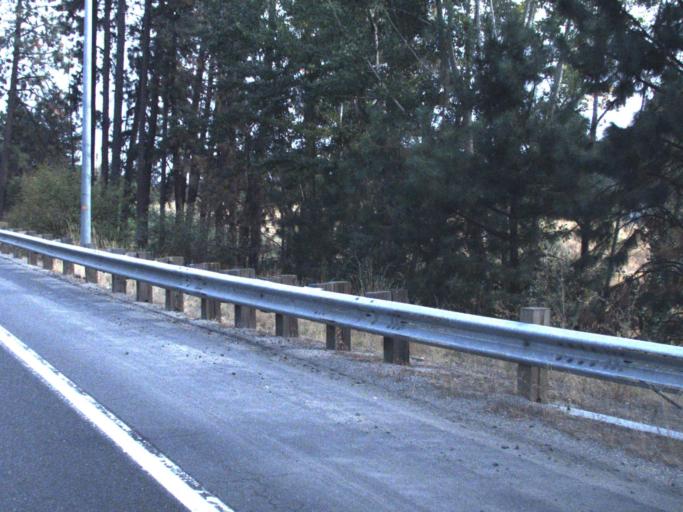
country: US
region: Washington
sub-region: Spokane County
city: Mead
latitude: 47.7875
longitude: -117.3382
